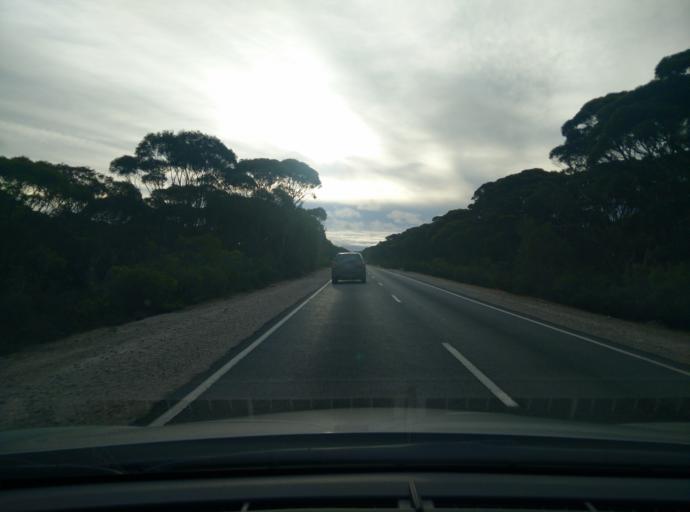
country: AU
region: South Australia
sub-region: Kangaroo Island
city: Kingscote
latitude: -35.8007
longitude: 137.8389
